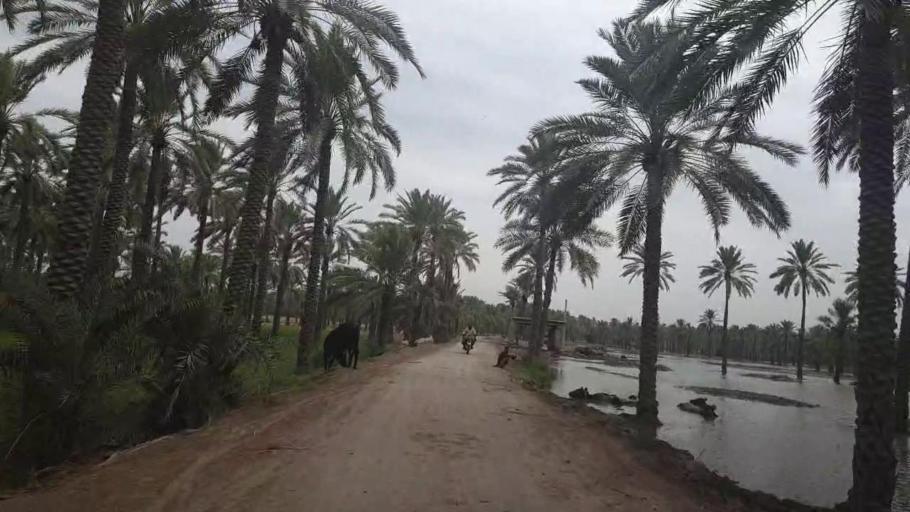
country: PK
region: Sindh
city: Khairpur
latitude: 27.5867
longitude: 68.7496
